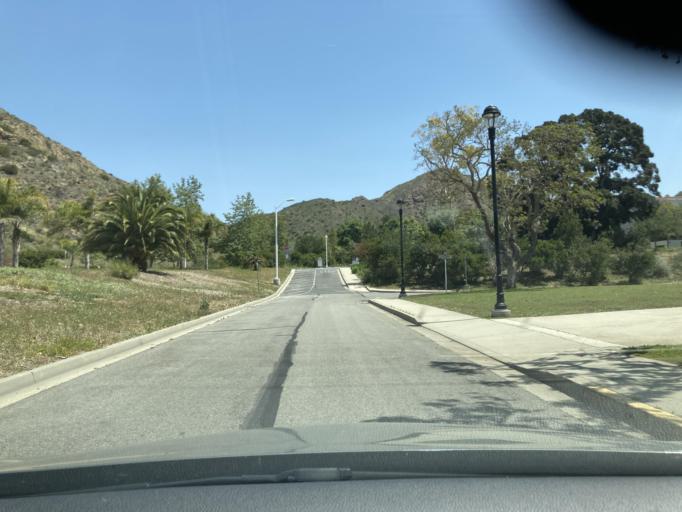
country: US
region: California
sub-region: Ventura County
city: Camarillo
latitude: 34.1639
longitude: -119.0410
